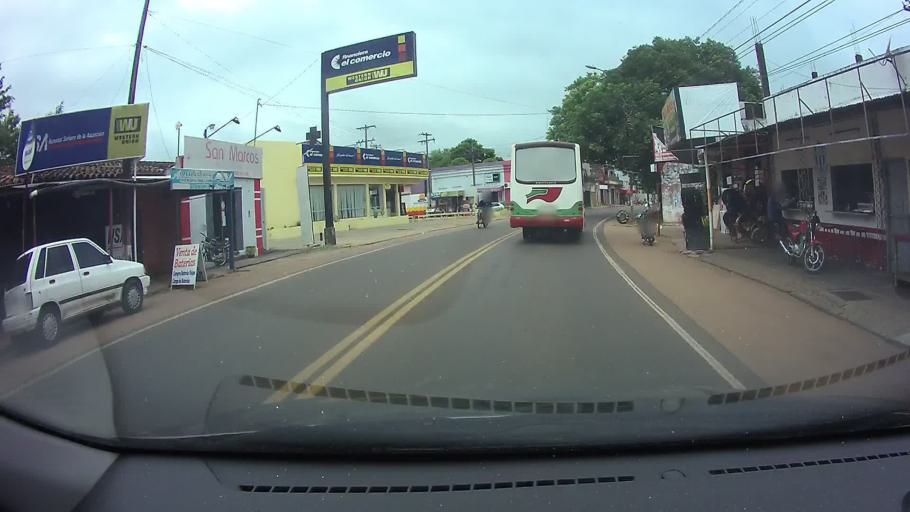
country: PY
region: Paraguari
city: Carapegua
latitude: -25.7694
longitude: -57.2438
